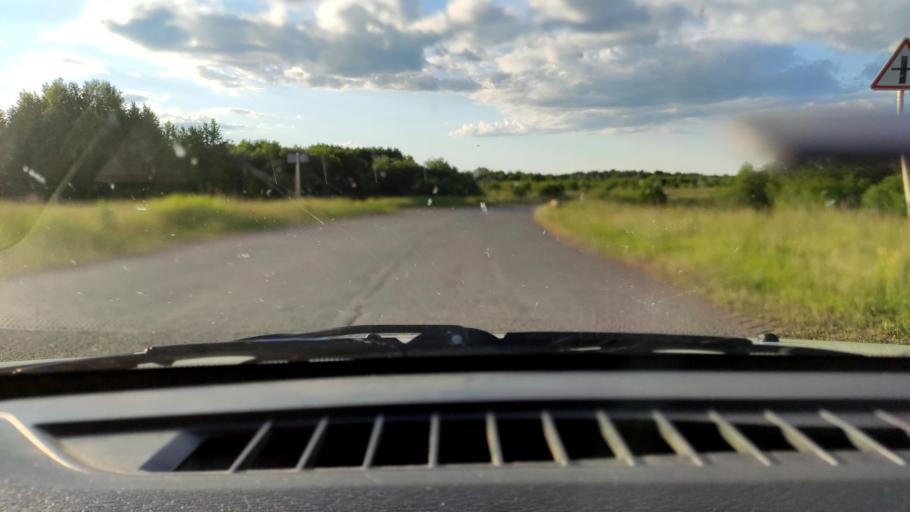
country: RU
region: Perm
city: Uinskoye
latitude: 57.0806
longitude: 56.5539
